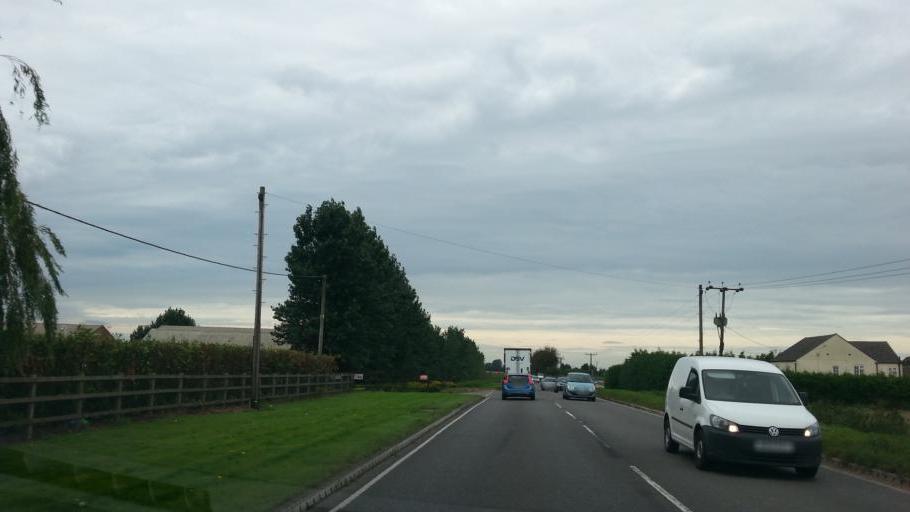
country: GB
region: England
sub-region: Cambridgeshire
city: March
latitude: 52.6100
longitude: 0.0359
